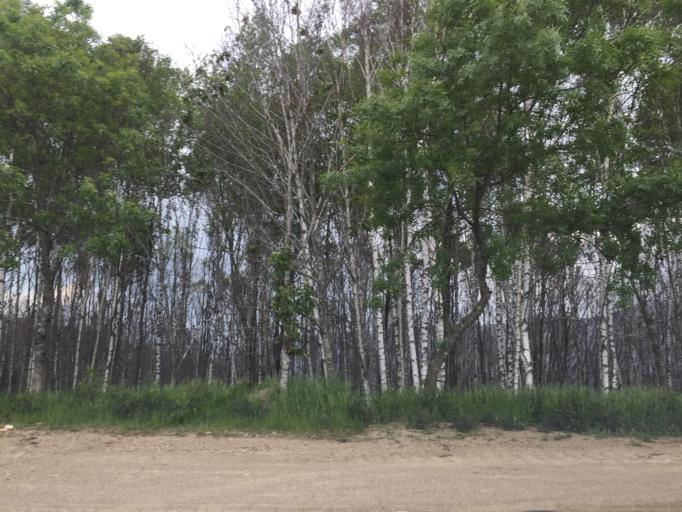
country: PT
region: Coimbra
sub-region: Arganil
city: Arganil
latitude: 40.1852
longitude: -7.9923
